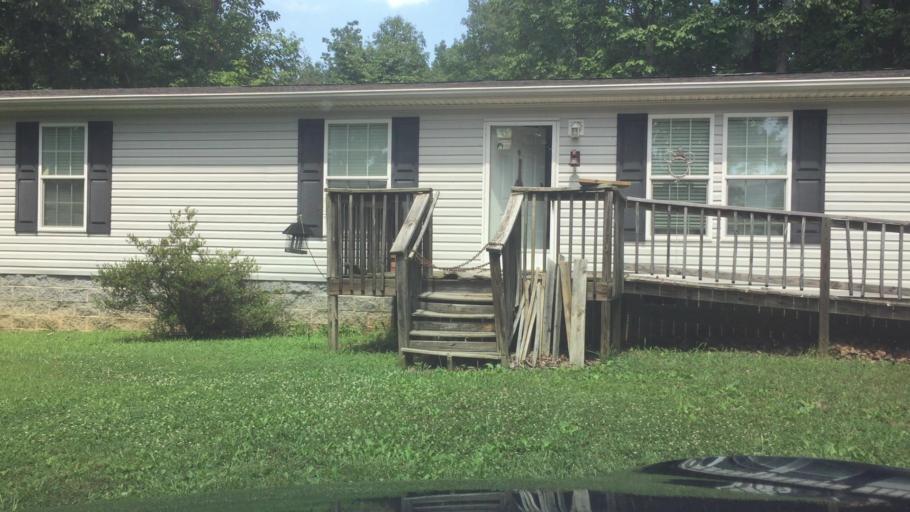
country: US
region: Virginia
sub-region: Appomattox County
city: Appomattox
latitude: 37.2843
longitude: -78.8505
